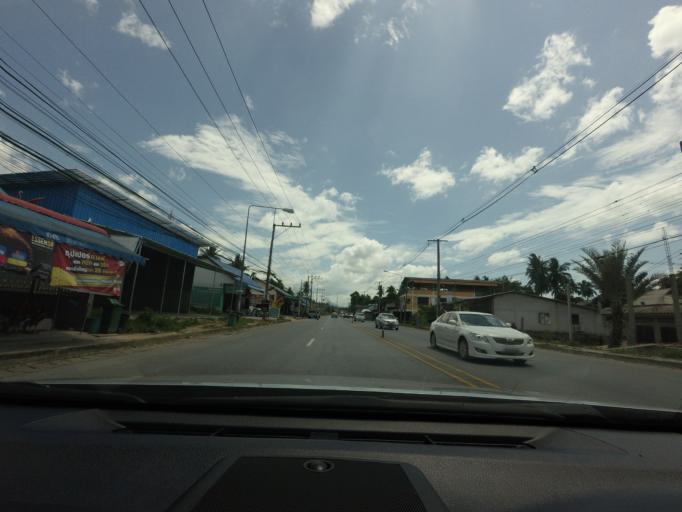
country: TH
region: Nakhon Si Thammarat
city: Tha Sala
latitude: 8.8970
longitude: 99.9007
